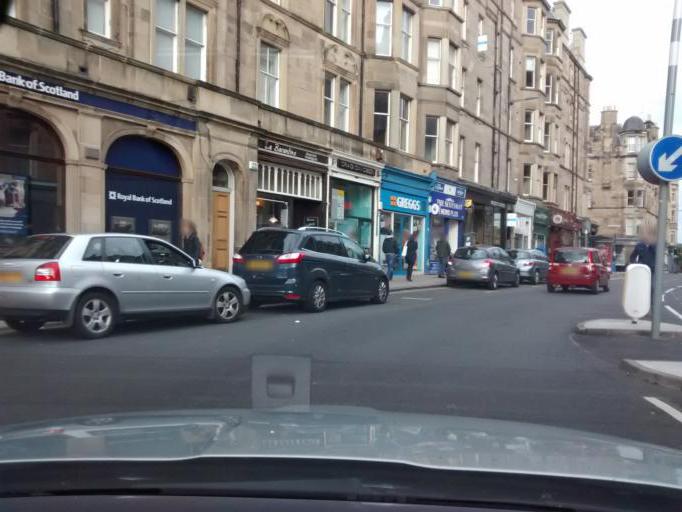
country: GB
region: Scotland
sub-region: Edinburgh
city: Edinburgh
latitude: 55.9357
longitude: -3.2100
